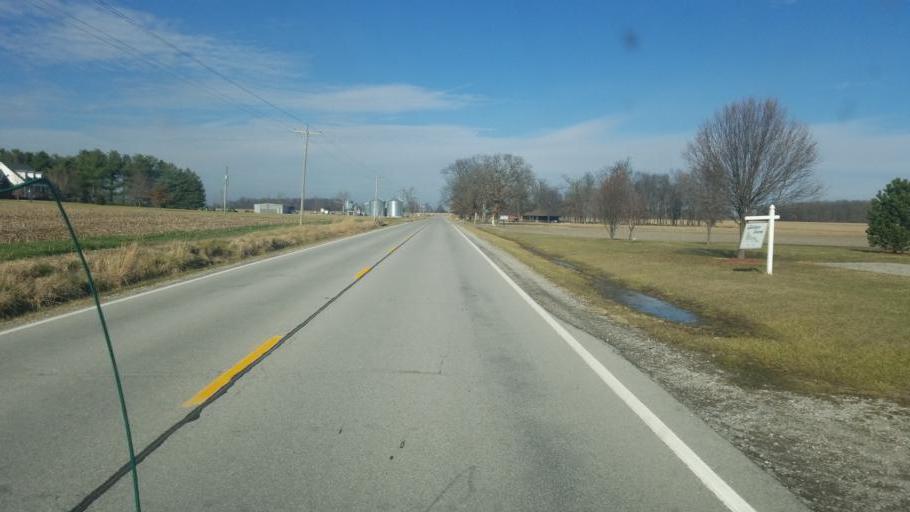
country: US
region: Illinois
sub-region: Saline County
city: Eldorado
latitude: 37.8986
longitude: -88.4530
